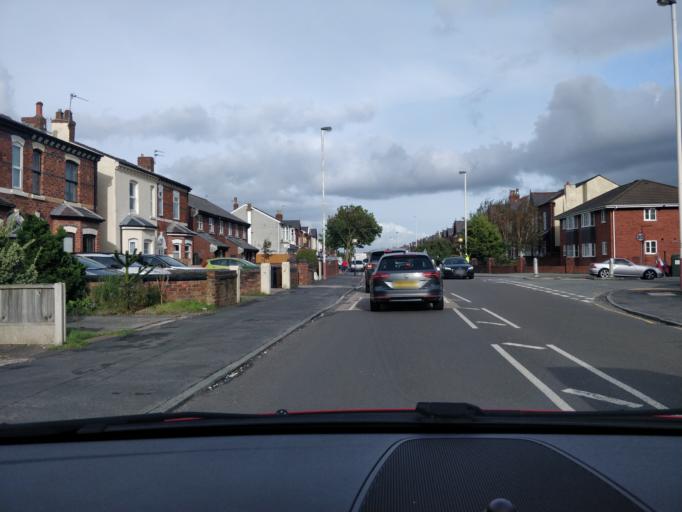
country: GB
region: England
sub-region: Sefton
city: Southport
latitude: 53.6312
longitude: -3.0077
